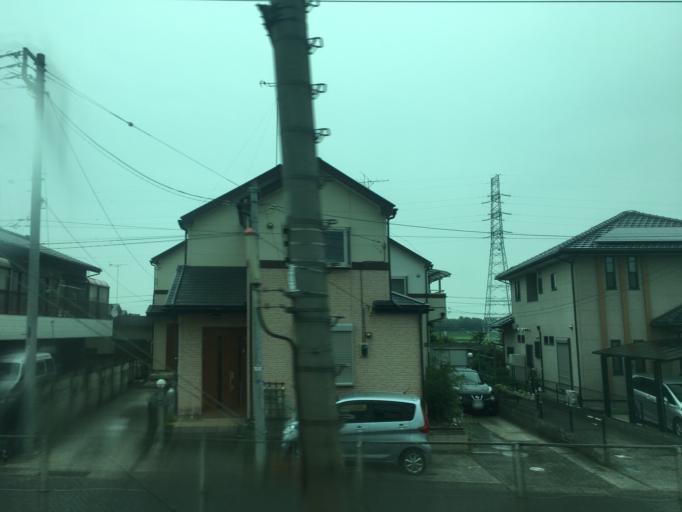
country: JP
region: Ibaraki
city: Koga
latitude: 36.1625
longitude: 139.7187
